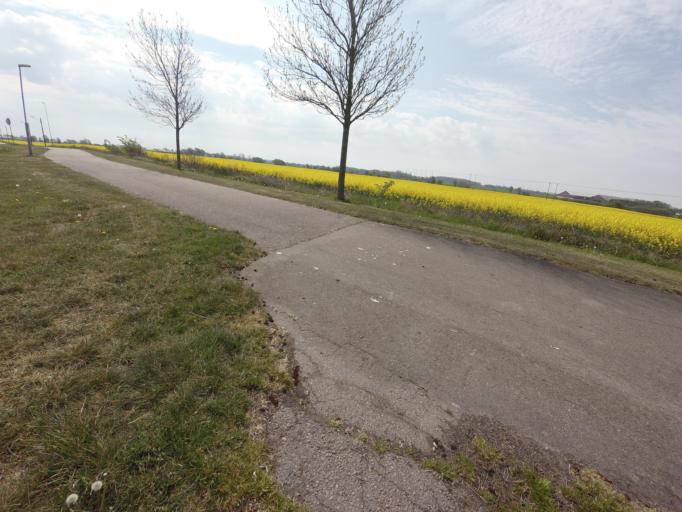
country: SE
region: Skane
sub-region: Hoganas Kommun
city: Hoganas
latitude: 56.2009
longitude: 12.5940
